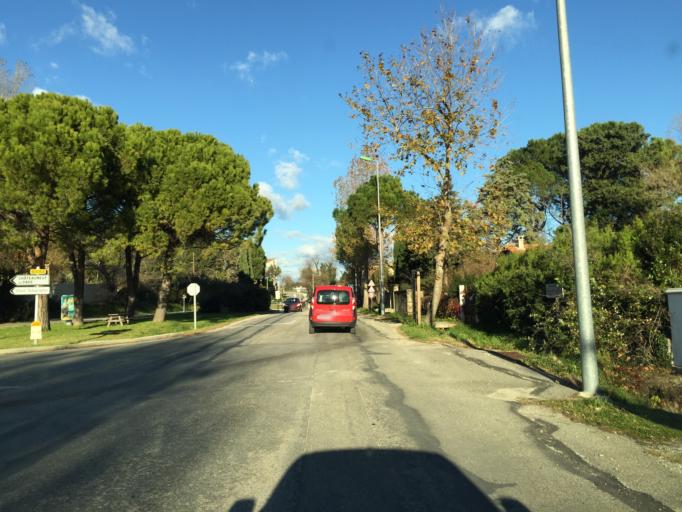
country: FR
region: Provence-Alpes-Cote d'Azur
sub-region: Departement du Vaucluse
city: Bedarrides
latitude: 44.0414
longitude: 4.8844
